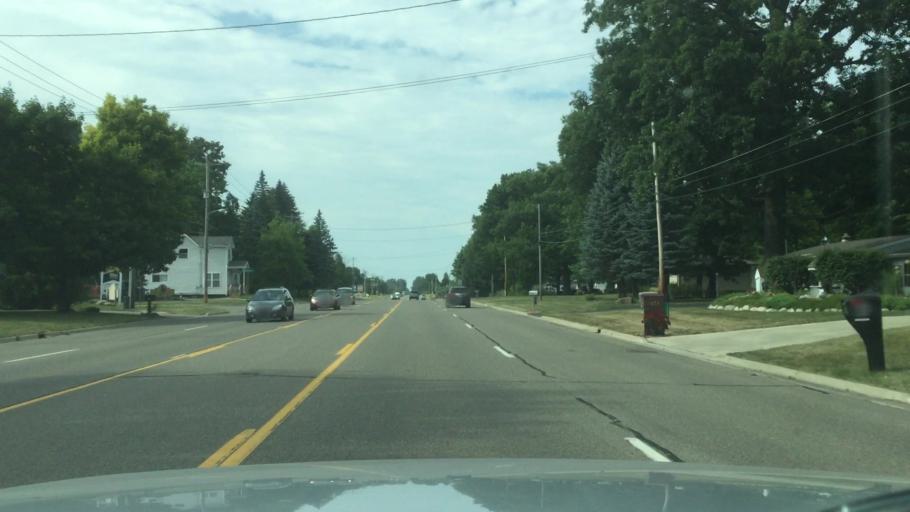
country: US
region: Michigan
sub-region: Genesee County
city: Swartz Creek
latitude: 43.0086
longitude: -83.8121
